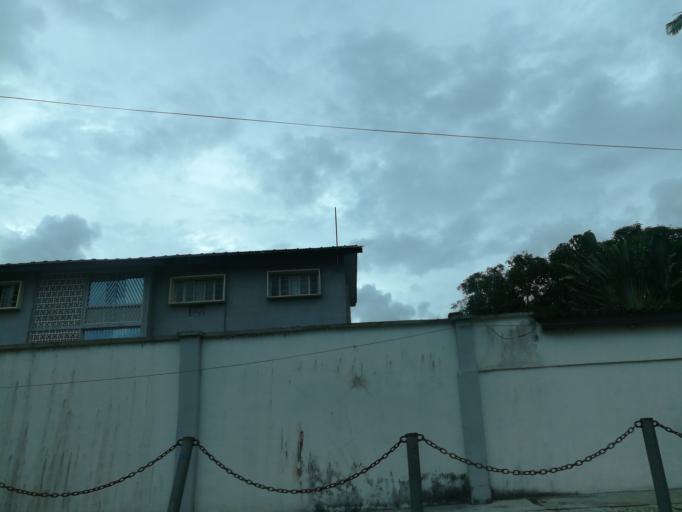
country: NG
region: Lagos
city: Lagos
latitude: 6.4334
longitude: 3.4114
